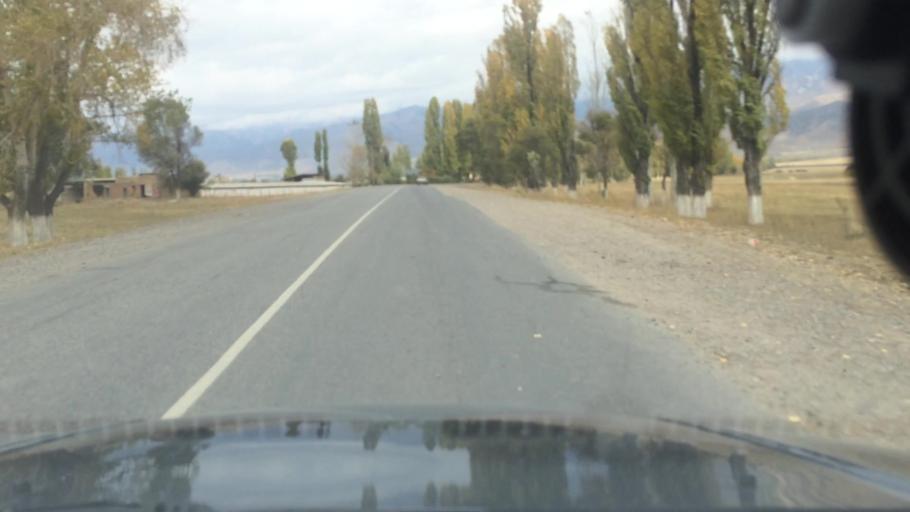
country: KG
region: Ysyk-Koel
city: Tyup
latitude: 42.7418
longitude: 78.3411
